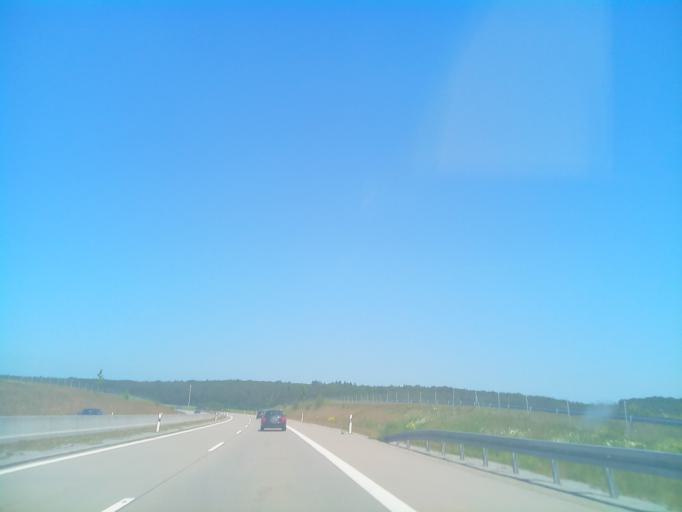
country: DE
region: Bavaria
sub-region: Regierungsbezirk Unterfranken
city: Strahlungen
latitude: 50.2712
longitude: 10.2420
